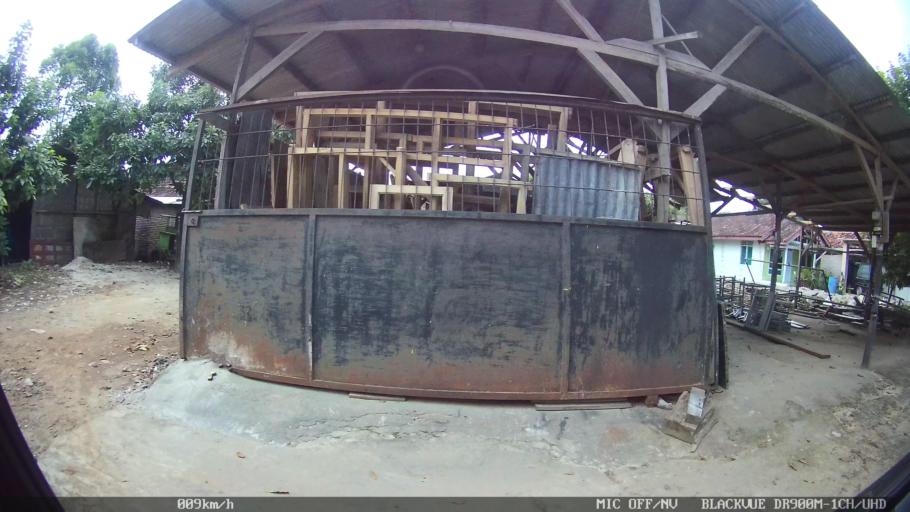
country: ID
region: Lampung
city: Kedaton
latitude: -5.3954
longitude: 105.2100
